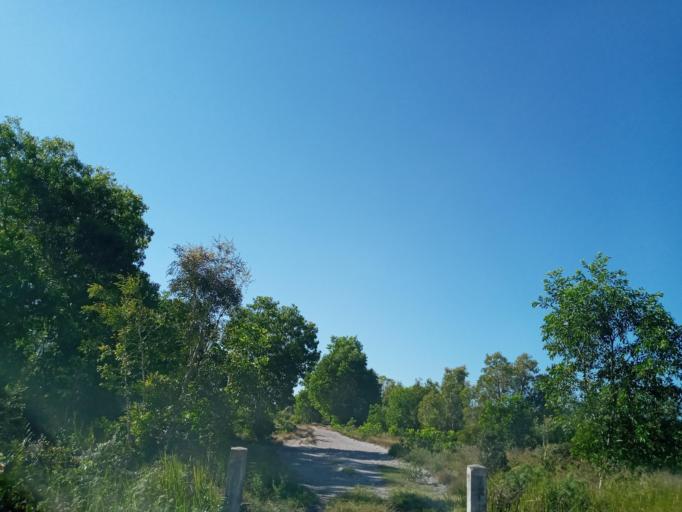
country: MG
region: Anosy
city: Fort Dauphin
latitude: -24.9064
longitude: 47.0975
